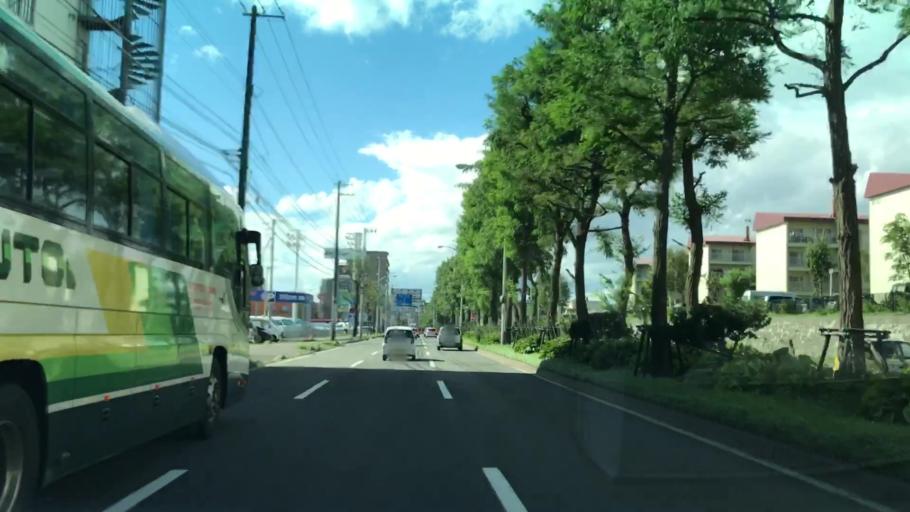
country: JP
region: Hokkaido
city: Sapporo
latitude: 43.0314
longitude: 141.4320
